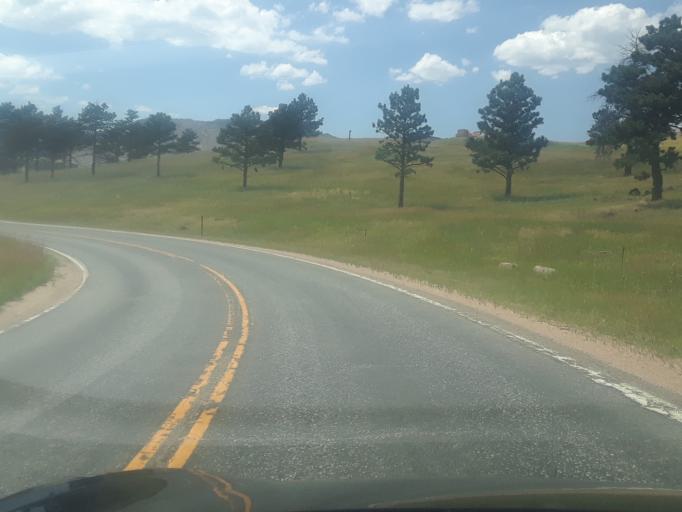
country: US
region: Colorado
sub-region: Boulder County
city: Boulder
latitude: 40.0512
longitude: -105.3451
